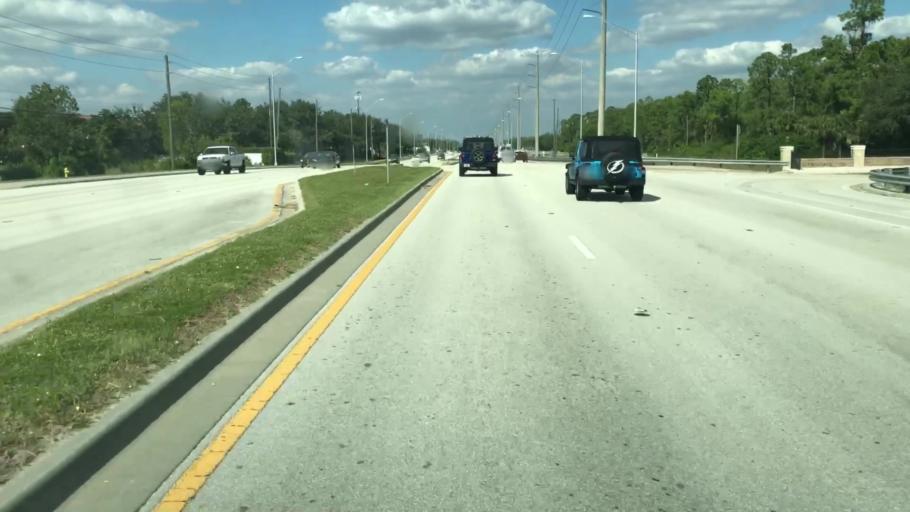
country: US
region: Florida
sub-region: Collier County
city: Vineyards
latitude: 26.2520
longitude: -81.6884
